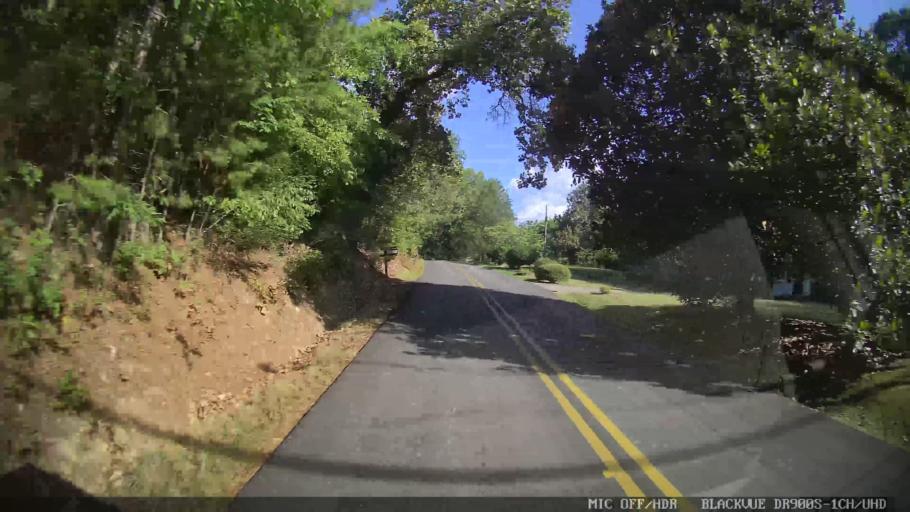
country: US
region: Georgia
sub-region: Floyd County
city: Rome
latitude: 34.2177
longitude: -85.1314
